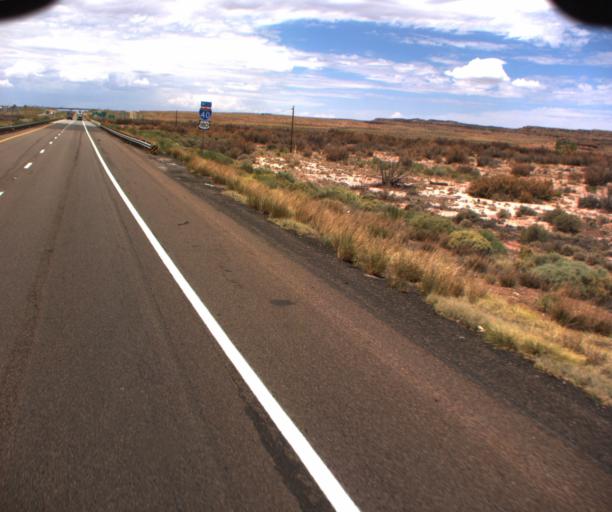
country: US
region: Arizona
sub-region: Navajo County
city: Holbrook
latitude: 34.9057
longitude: -110.1972
